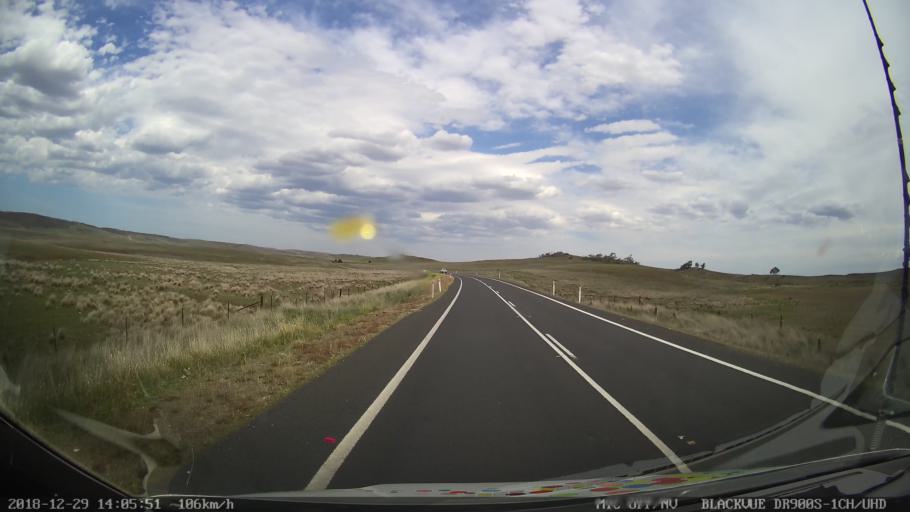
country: AU
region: New South Wales
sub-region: Cooma-Monaro
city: Cooma
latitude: -36.3364
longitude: 149.1947
